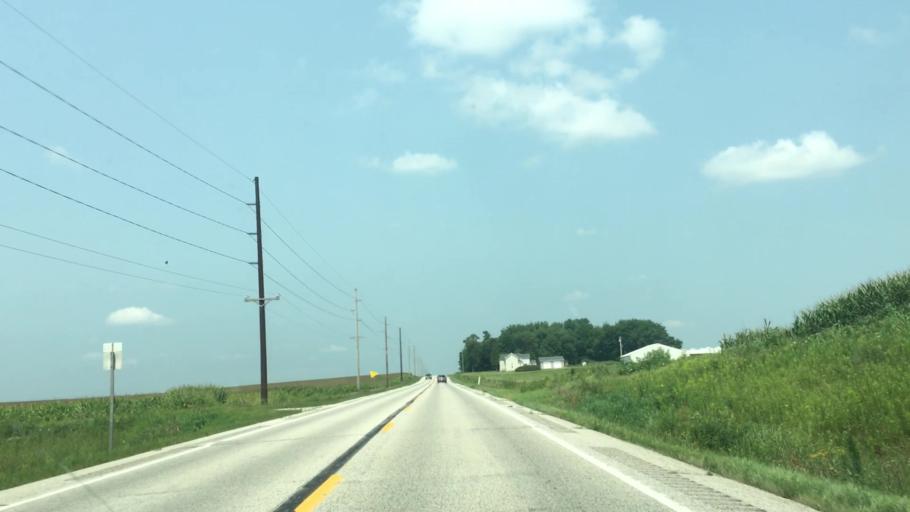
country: US
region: Iowa
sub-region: Buchanan County
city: Independence
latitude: 42.5552
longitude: -91.9048
